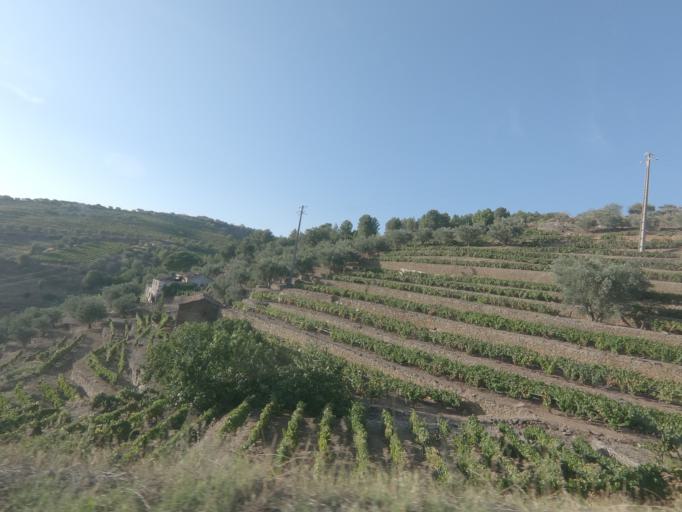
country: PT
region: Vila Real
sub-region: Sabrosa
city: Sabrosa
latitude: 41.2652
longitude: -7.5325
